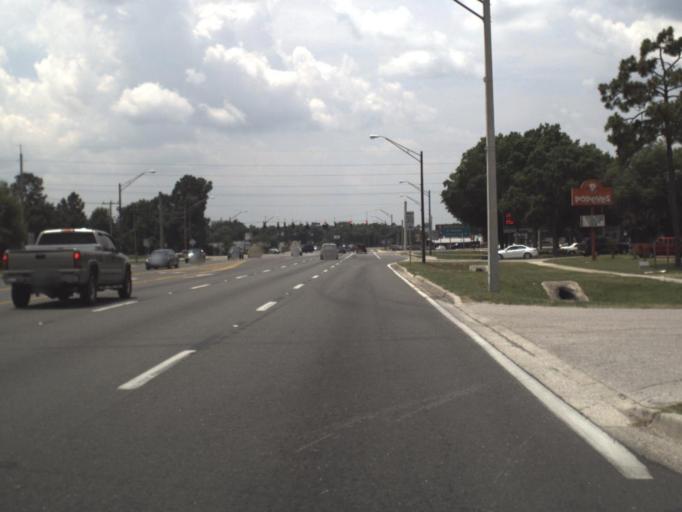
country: US
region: Florida
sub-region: Putnam County
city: Palatka
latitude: 29.6432
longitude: -81.6756
